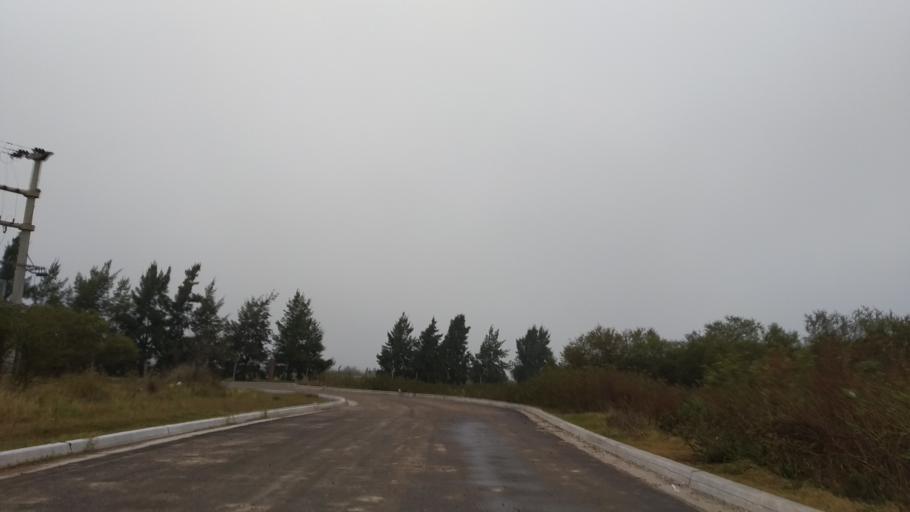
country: AR
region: Santa Fe
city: Funes
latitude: -32.9369
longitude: -60.7678
